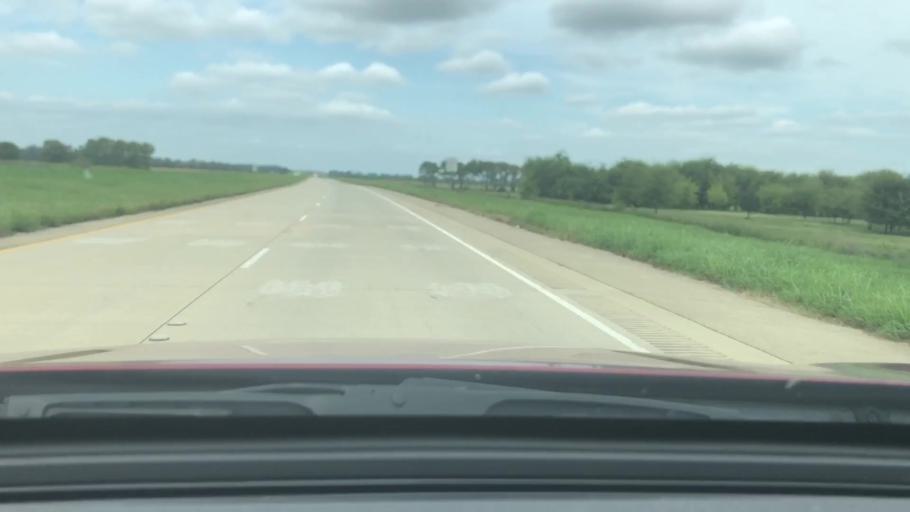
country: US
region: Louisiana
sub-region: Caddo Parish
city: Vivian
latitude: 32.8642
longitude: -93.8620
